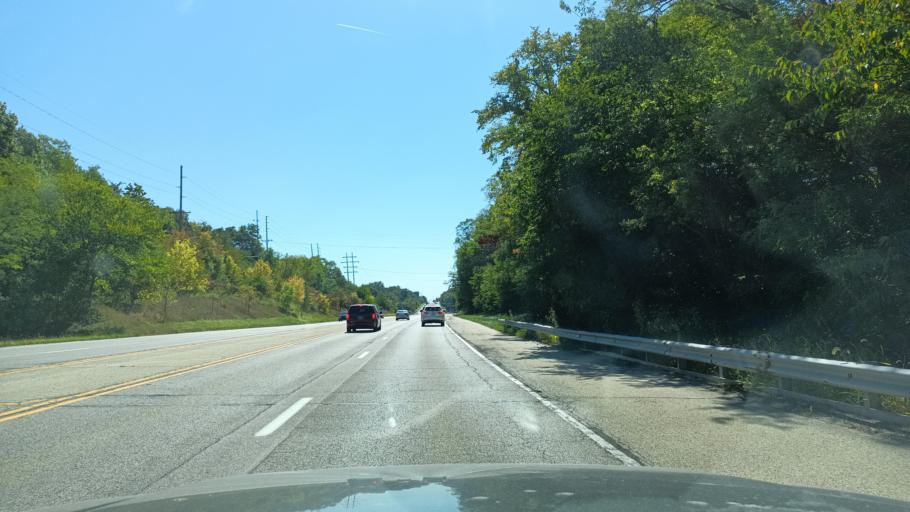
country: US
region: Illinois
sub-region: Peoria County
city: Peoria Heights
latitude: 40.7635
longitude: -89.6410
